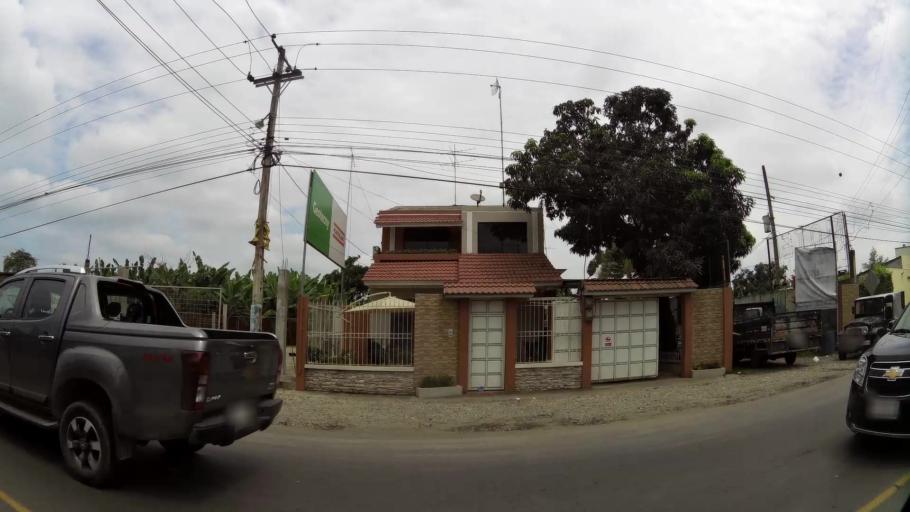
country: EC
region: El Oro
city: Machala
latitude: -3.2933
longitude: -79.9030
